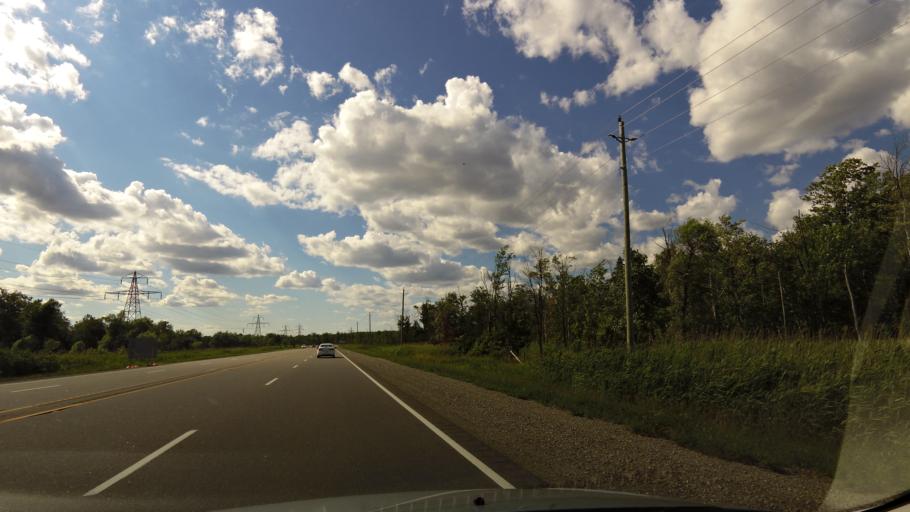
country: CA
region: Ontario
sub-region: Halton
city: Milton
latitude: 43.4059
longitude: -80.0437
